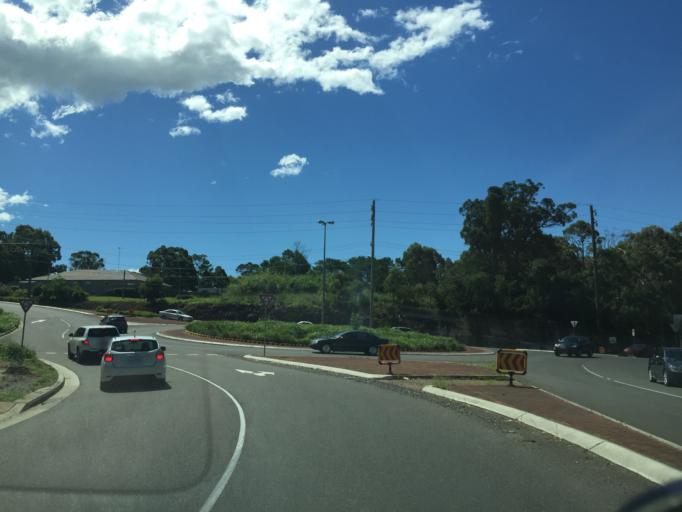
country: AU
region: New South Wales
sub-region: The Hills Shire
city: Beaumont Hills
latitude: -33.6974
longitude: 150.9688
